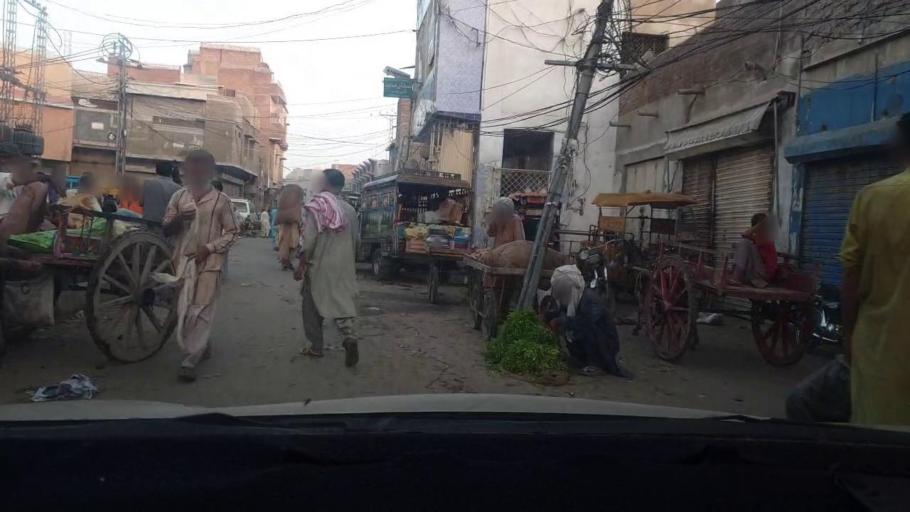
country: PK
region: Sindh
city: Larkana
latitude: 27.5587
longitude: 68.2199
